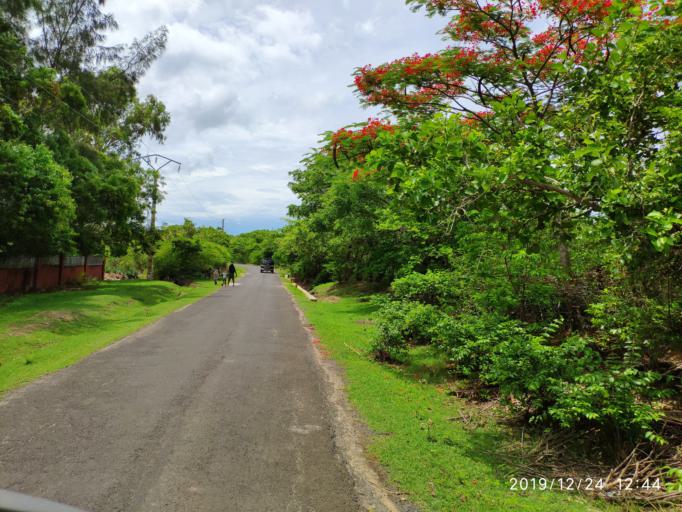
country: MG
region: Diana
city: Antsiranana
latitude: -12.2740
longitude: 49.3539
